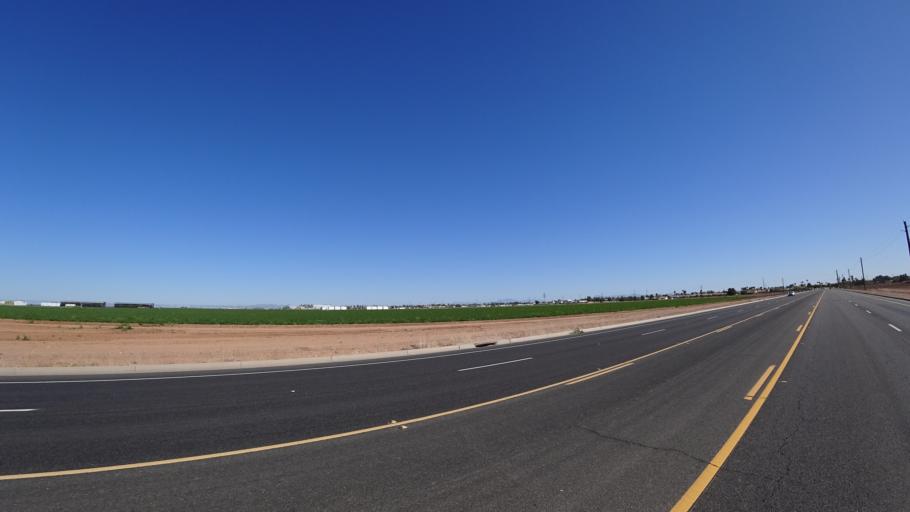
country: US
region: Arizona
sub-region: Maricopa County
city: Sun Lakes
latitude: 33.2192
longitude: -111.8990
